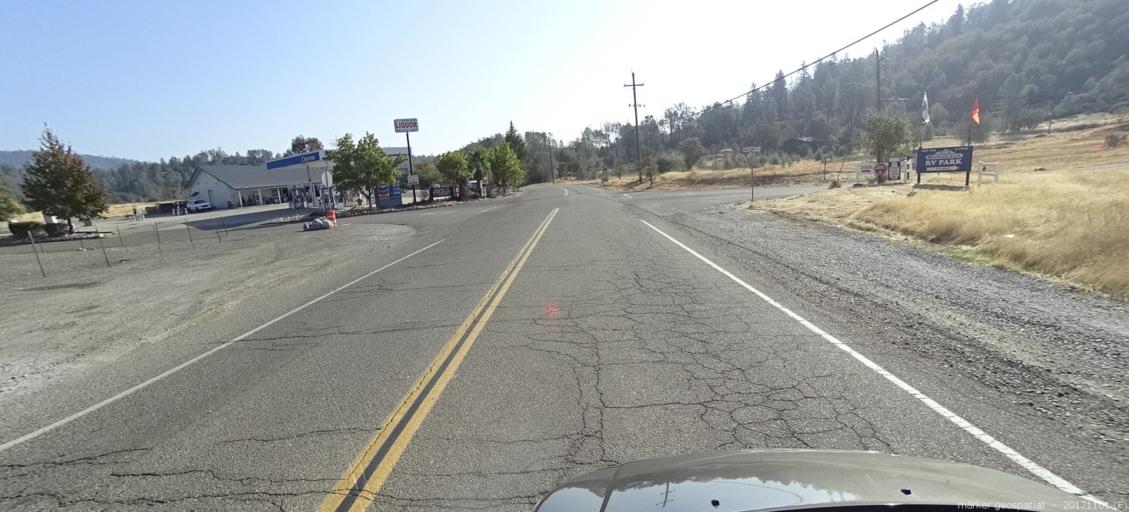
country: US
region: California
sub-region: Shasta County
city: Shasta Lake
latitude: 40.7052
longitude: -122.3356
